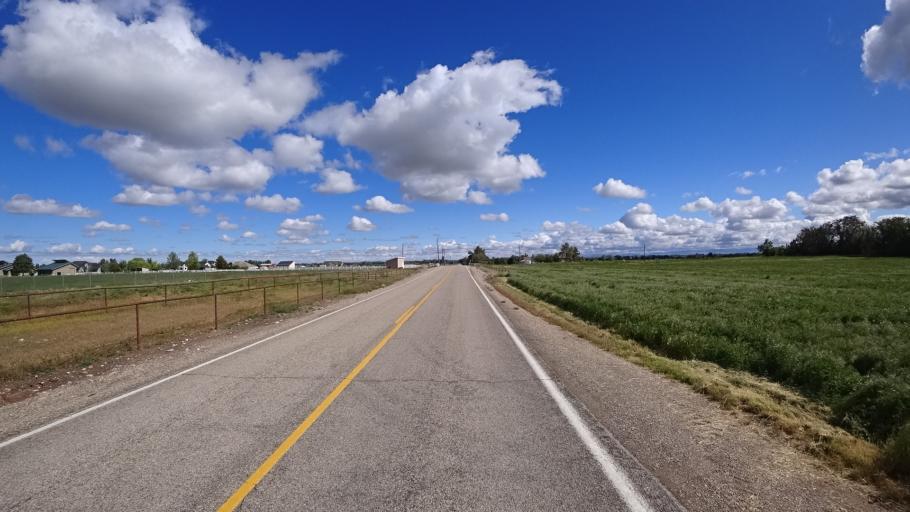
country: US
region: Idaho
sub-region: Ada County
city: Kuna
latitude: 43.5195
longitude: -116.4736
